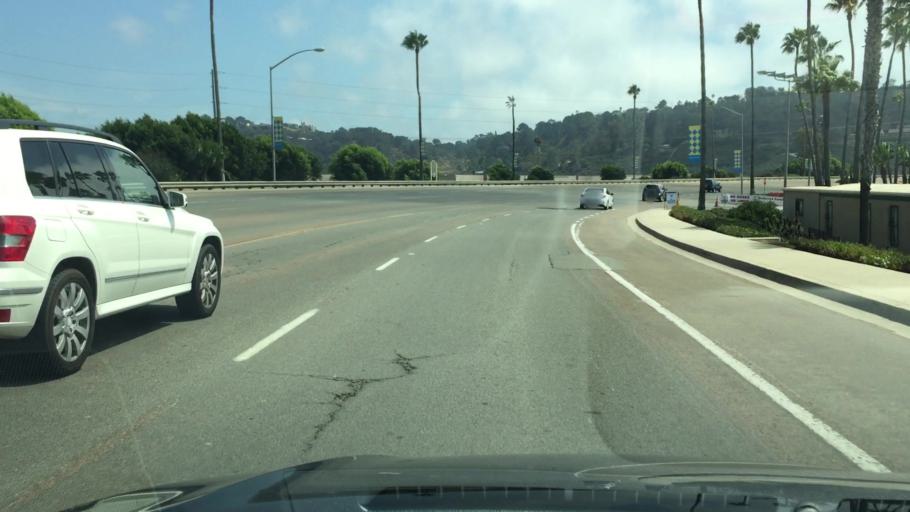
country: US
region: California
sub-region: San Diego County
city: Del Mar
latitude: 32.9744
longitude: -117.2563
